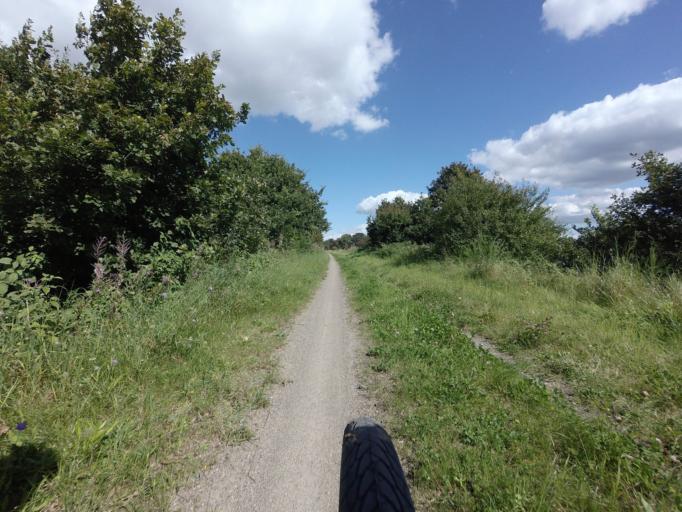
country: DK
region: South Denmark
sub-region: Vejle Kommune
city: Give
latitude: 55.9995
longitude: 9.3374
